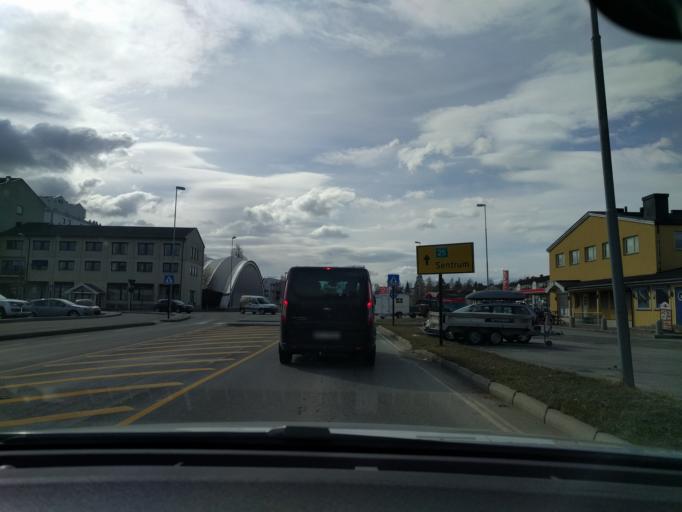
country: NO
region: Hedmark
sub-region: Hamar
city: Hamar
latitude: 60.7968
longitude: 11.0893
